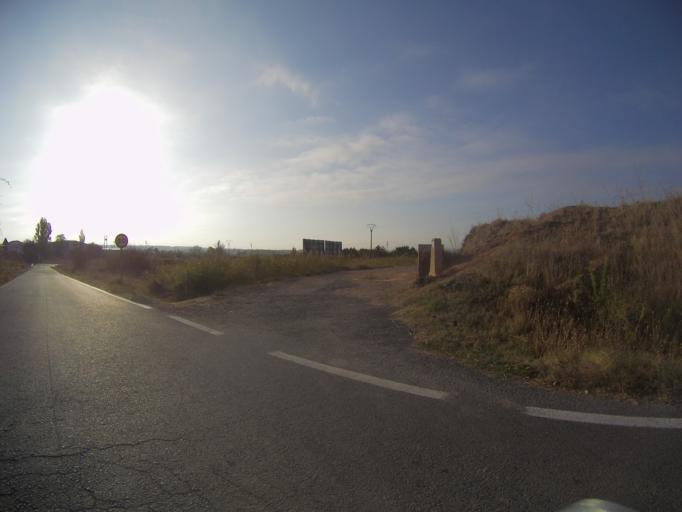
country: ES
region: Navarre
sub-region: Provincia de Navarra
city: Viana
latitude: 42.5114
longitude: -2.3797
